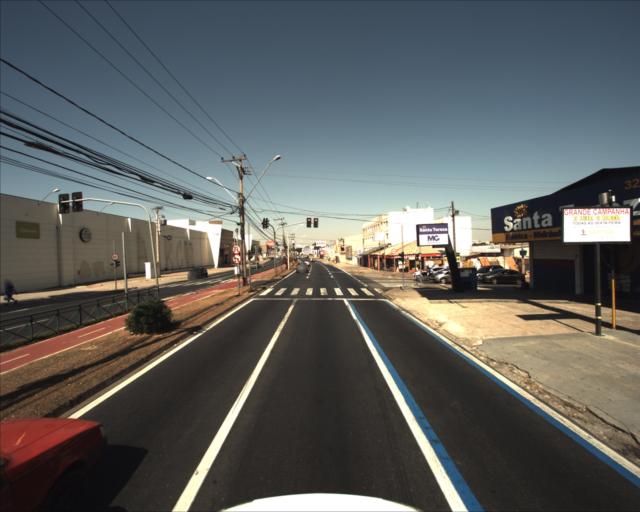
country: BR
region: Sao Paulo
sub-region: Sorocaba
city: Sorocaba
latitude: -23.4648
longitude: -47.4791
